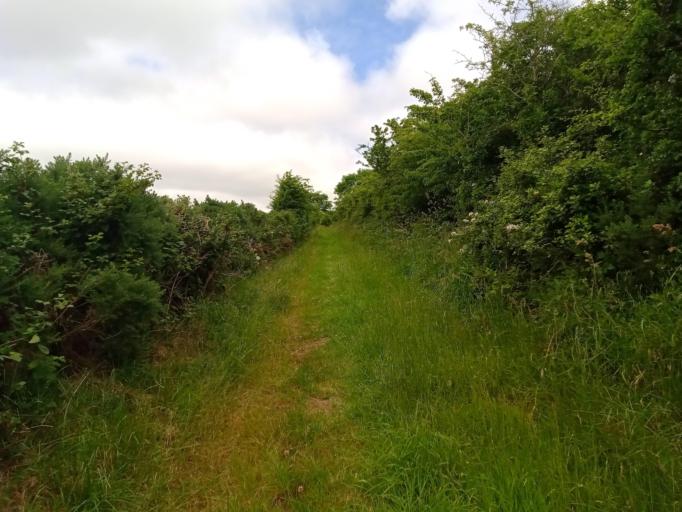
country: IE
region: Leinster
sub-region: Kilkenny
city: Ballyragget
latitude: 52.7916
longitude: -7.4547
